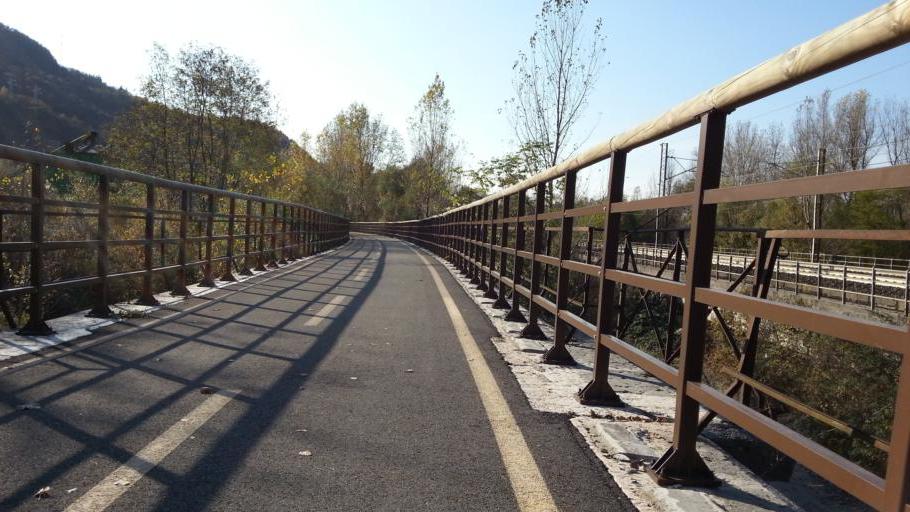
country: IT
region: Friuli Venezia Giulia
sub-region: Provincia di Udine
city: Venzone
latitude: 46.3146
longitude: 13.1277
